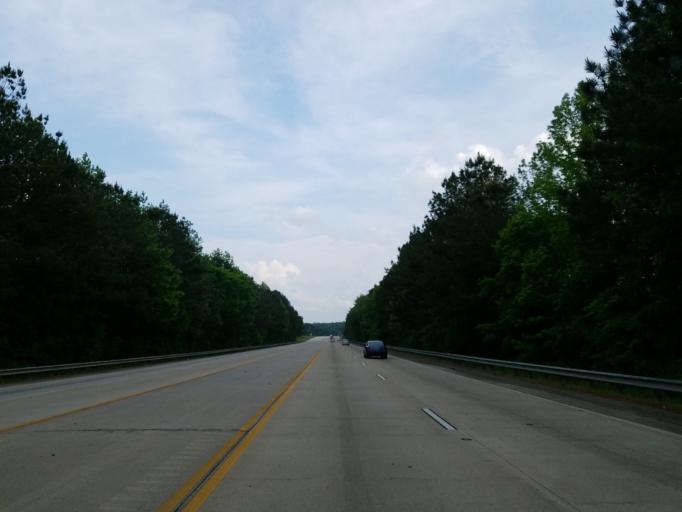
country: US
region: Georgia
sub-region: Douglas County
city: Lithia Springs
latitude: 33.8250
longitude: -84.6637
